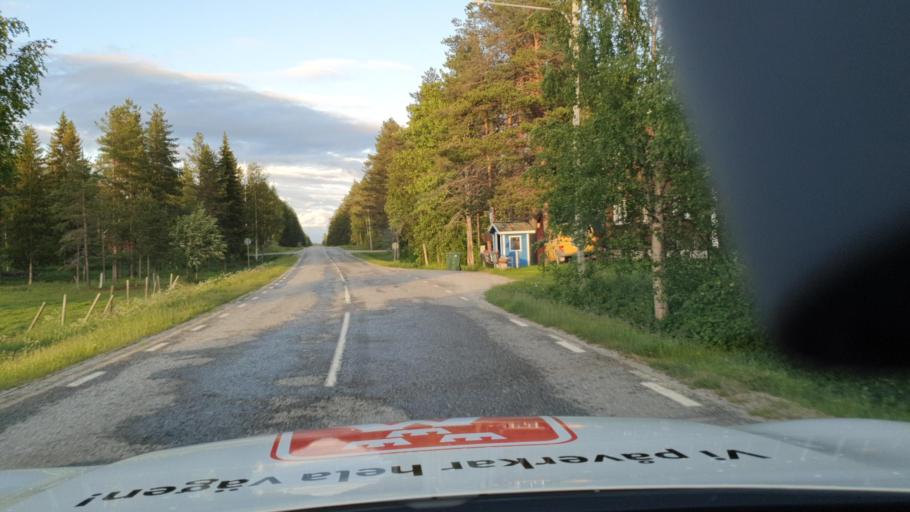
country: SE
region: Vaesterbotten
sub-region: Lycksele Kommun
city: Soderfors
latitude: 64.6260
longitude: 18.0716
